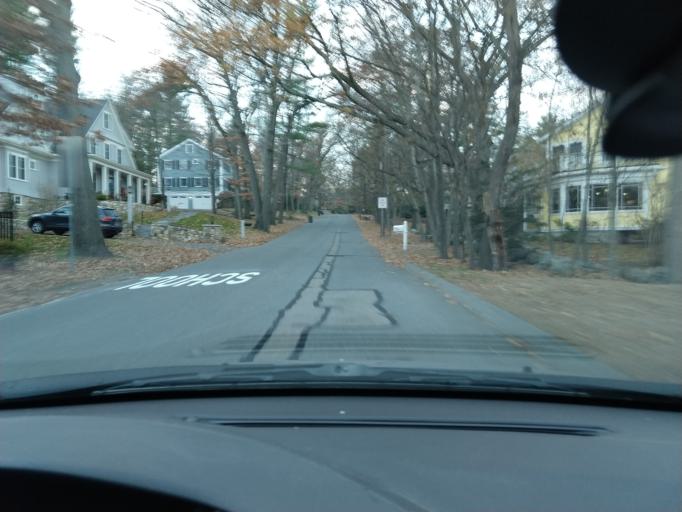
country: US
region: Massachusetts
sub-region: Middlesex County
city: Lexington
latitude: 42.4636
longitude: -71.2330
